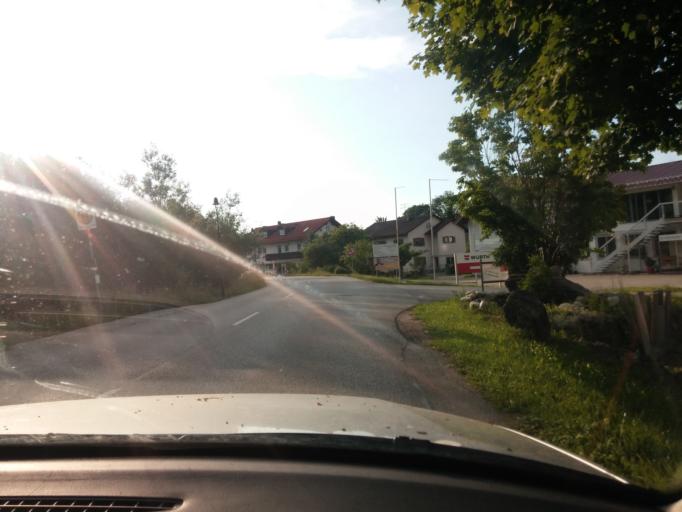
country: DE
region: Bavaria
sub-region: Upper Bavaria
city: Ebersberg
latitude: 48.0797
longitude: 11.9875
